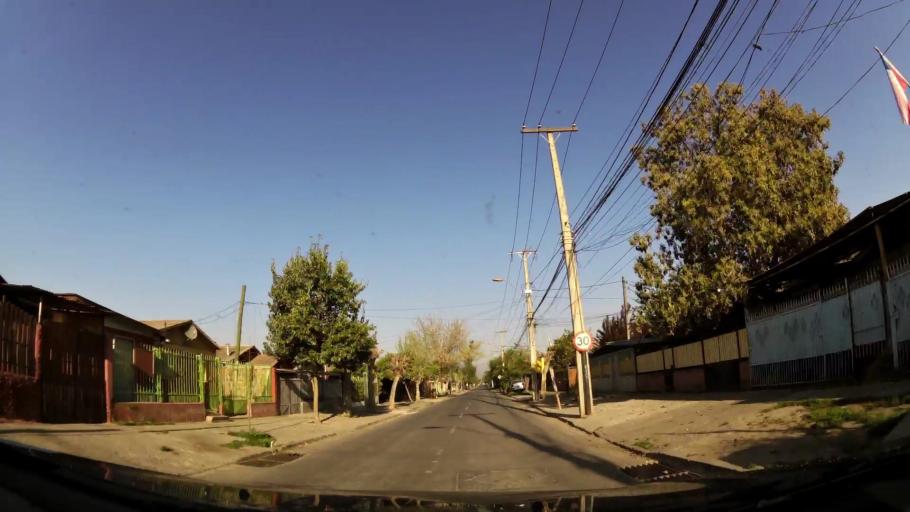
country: CL
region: Santiago Metropolitan
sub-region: Provincia de Santiago
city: Santiago
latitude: -33.3783
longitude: -70.6291
